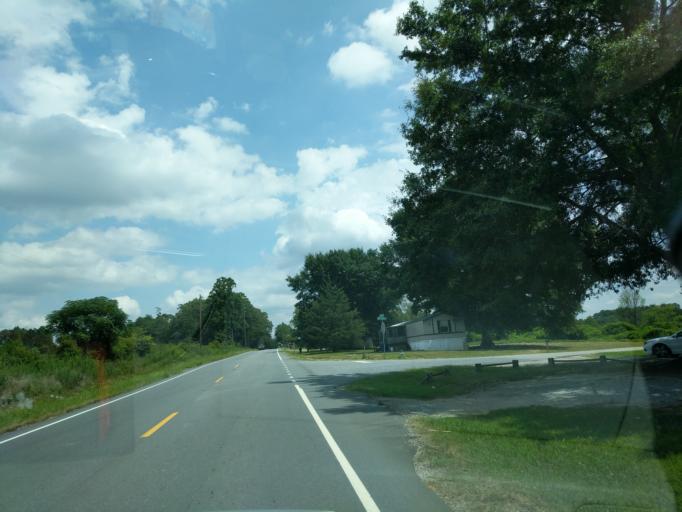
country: US
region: South Carolina
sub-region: Spartanburg County
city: Inman Mills
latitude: 34.9978
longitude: -82.1217
